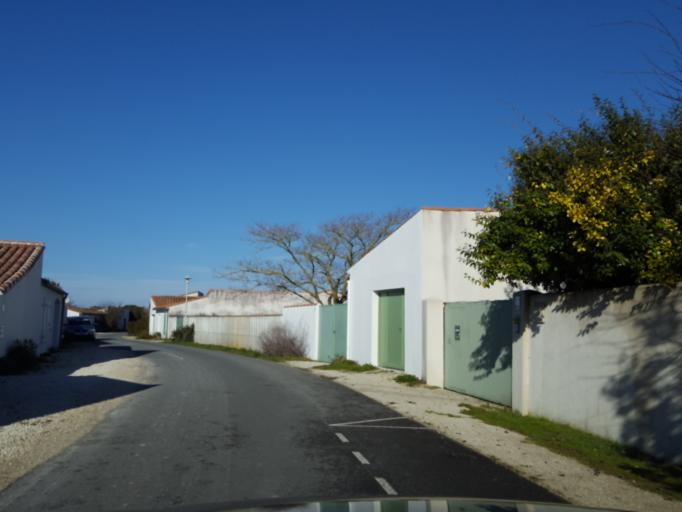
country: FR
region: Poitou-Charentes
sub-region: Departement de la Charente-Maritime
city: La Couarde-sur-Mer
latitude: 46.2181
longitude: -1.4397
